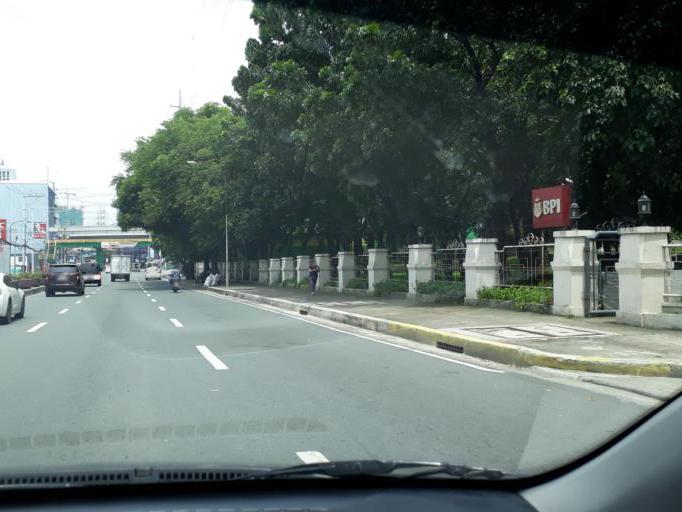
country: PH
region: Calabarzon
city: Del Monte
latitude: 14.6186
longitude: 121.0126
